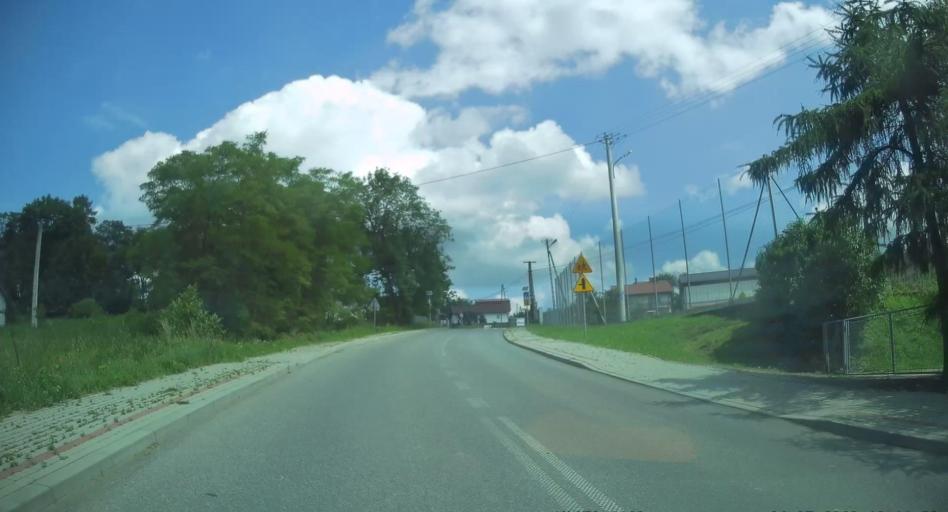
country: PL
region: Lesser Poland Voivodeship
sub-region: Powiat nowosadecki
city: Korzenna
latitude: 49.6866
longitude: 20.7752
